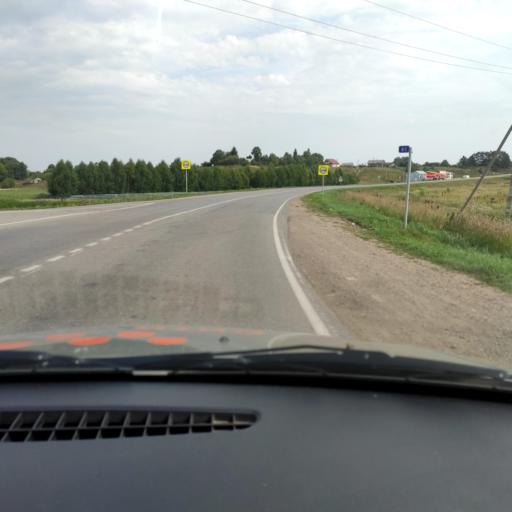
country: RU
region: Bashkortostan
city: Krasnaya Gorka
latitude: 55.1777
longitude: 56.6669
